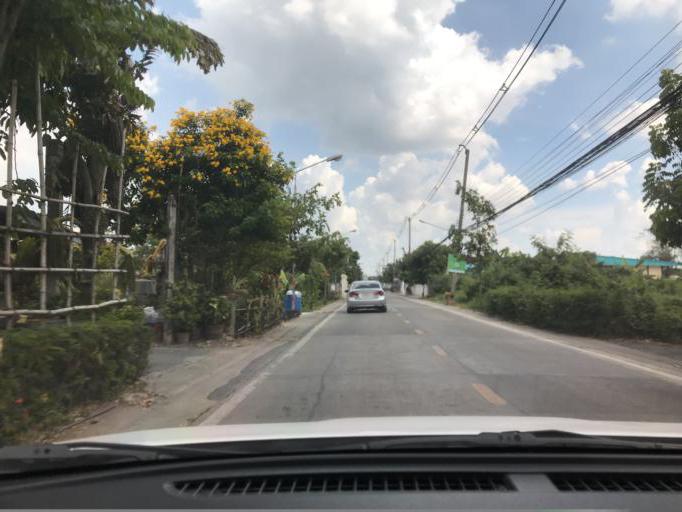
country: TH
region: Phra Nakhon Si Ayutthaya
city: Ban Bang Kadi Pathum Thani
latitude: 14.0042
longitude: 100.5476
